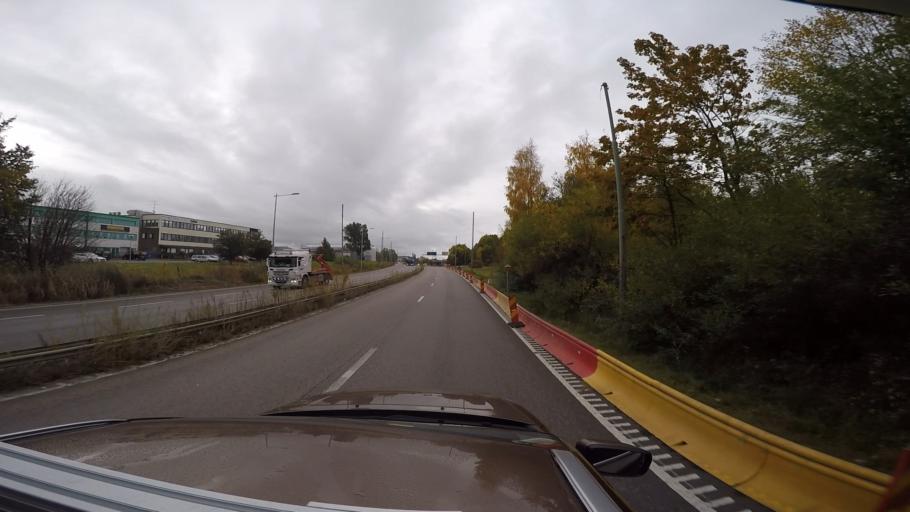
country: SE
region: Vaestra Goetaland
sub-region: Goteborg
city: Majorna
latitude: 57.6521
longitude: 11.9337
